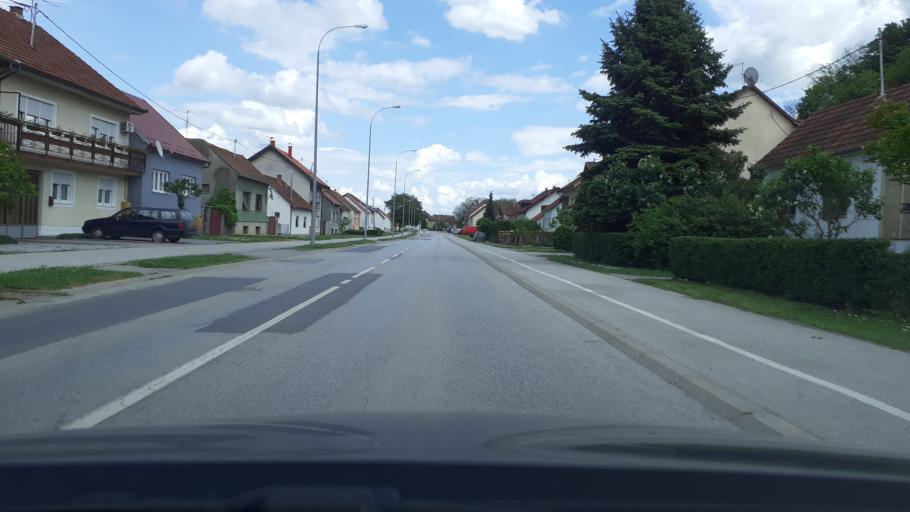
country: HR
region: Pozesko-Slavonska
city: Vidovci
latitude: 45.3341
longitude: 17.7026
